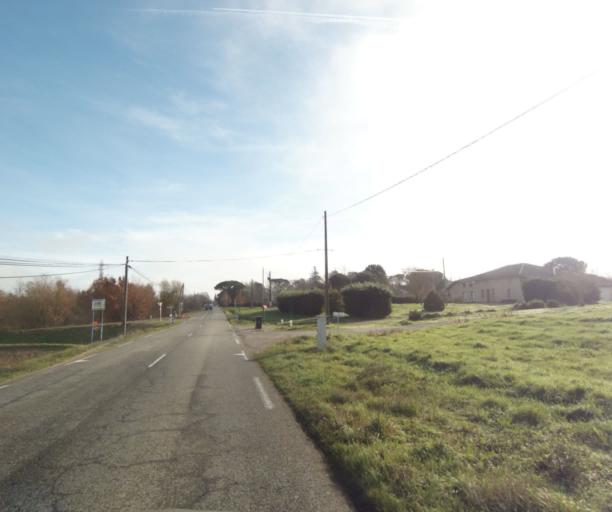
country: FR
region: Midi-Pyrenees
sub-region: Departement de la Haute-Garonne
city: Villemur-sur-Tarn
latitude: 43.8658
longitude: 1.4737
